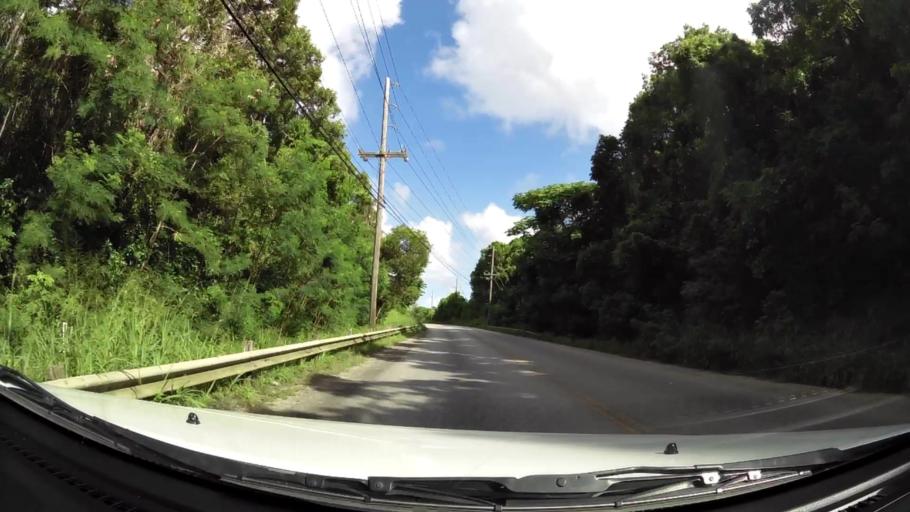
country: BB
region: Saint Peter
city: Speightstown
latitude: 13.2353
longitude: -59.6232
